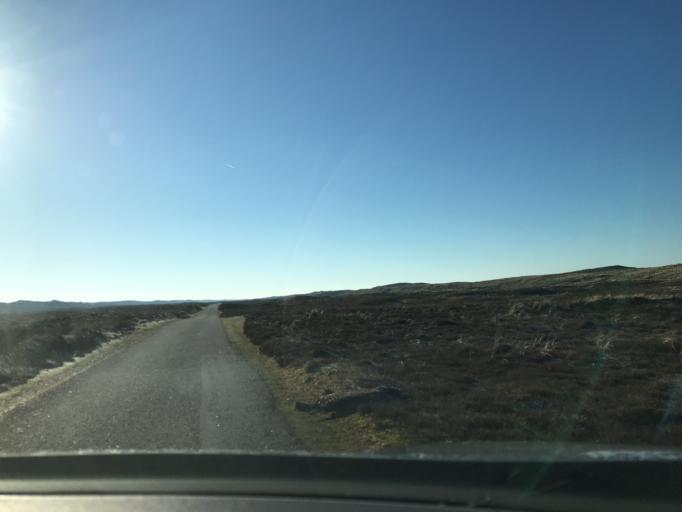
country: DK
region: South Denmark
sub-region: Varde Kommune
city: Oksbol
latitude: 55.7992
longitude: 8.1820
